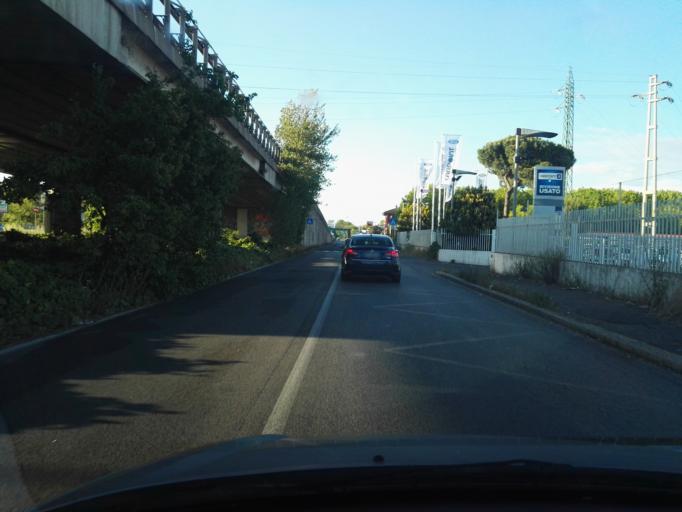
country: IT
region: Latium
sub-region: Citta metropolitana di Roma Capitale
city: Selcetta
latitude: 41.7934
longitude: 12.4523
